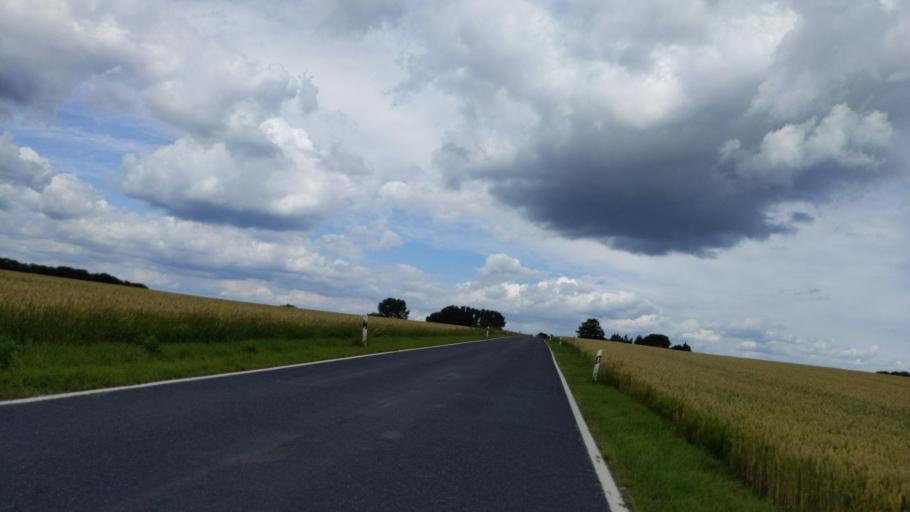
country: DE
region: Mecklenburg-Vorpommern
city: Dassow
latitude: 53.9487
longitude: 10.9738
